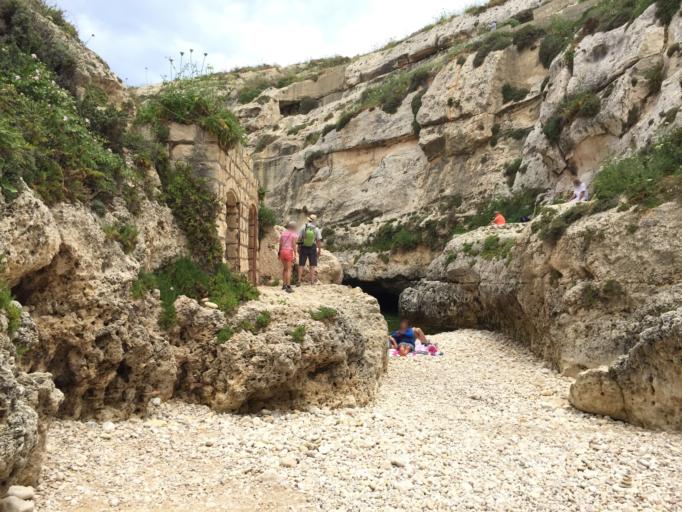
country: MT
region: Iz-Zebbug
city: Zebbug
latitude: 36.0786
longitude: 14.2282
